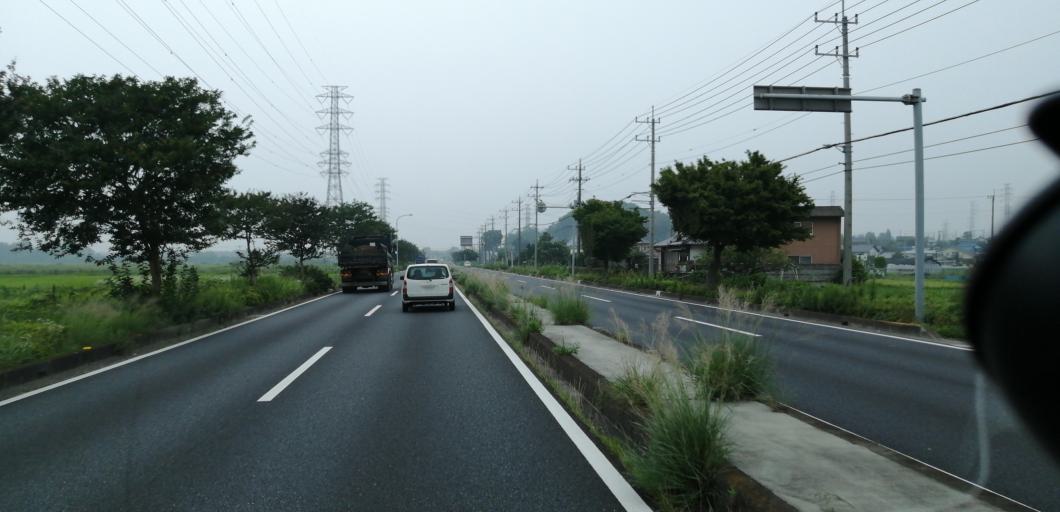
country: JP
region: Saitama
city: Fukayacho
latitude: 36.1504
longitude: 139.3200
